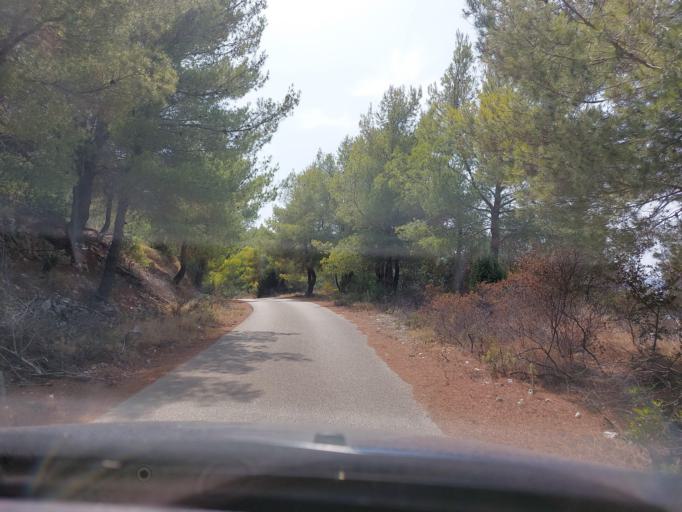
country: HR
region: Dubrovacko-Neretvanska
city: Smokvica
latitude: 42.7276
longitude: 16.8864
